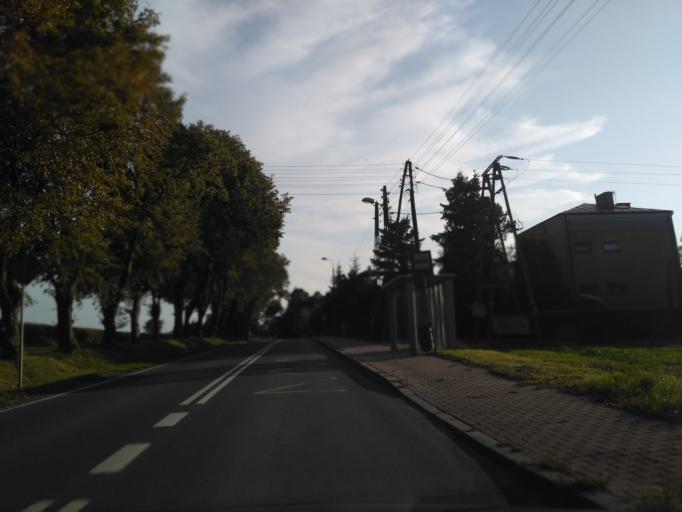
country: PL
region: Lublin Voivodeship
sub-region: Powiat lubelski
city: Bychawa
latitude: 51.0108
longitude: 22.5322
